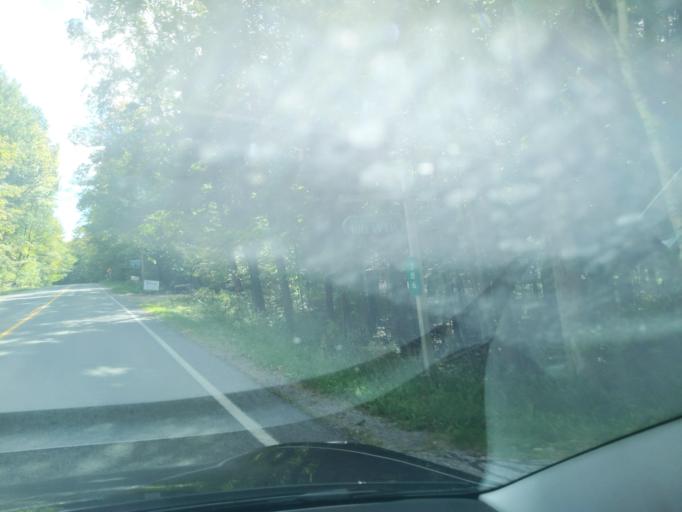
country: US
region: Michigan
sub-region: Antrim County
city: Bellaire
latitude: 45.0288
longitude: -85.2957
